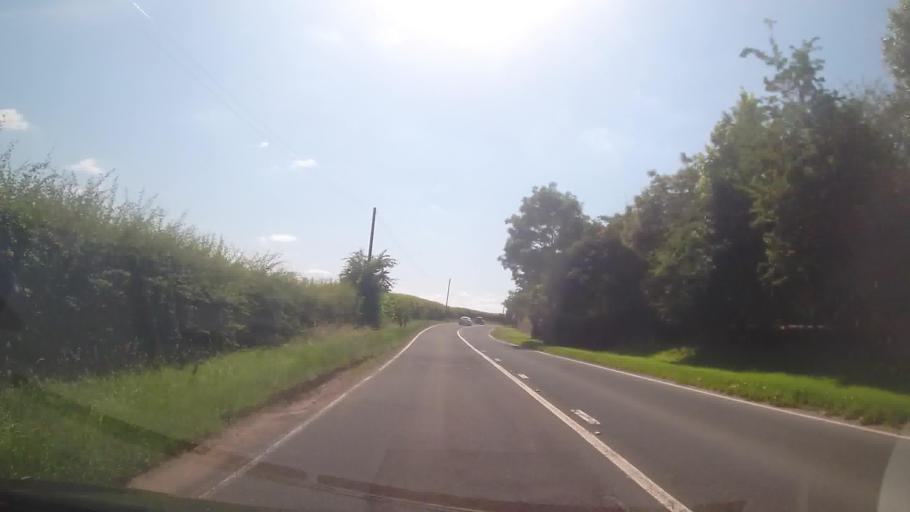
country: GB
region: England
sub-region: Herefordshire
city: Ocle Pychard
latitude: 52.0808
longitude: -2.5978
